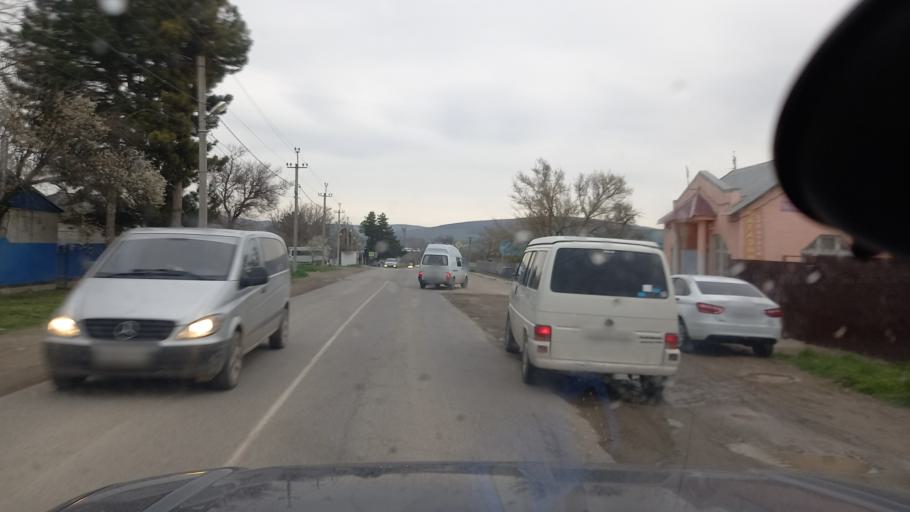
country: RU
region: Krasnodarskiy
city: Anapskaya
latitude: 44.8942
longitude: 37.4597
